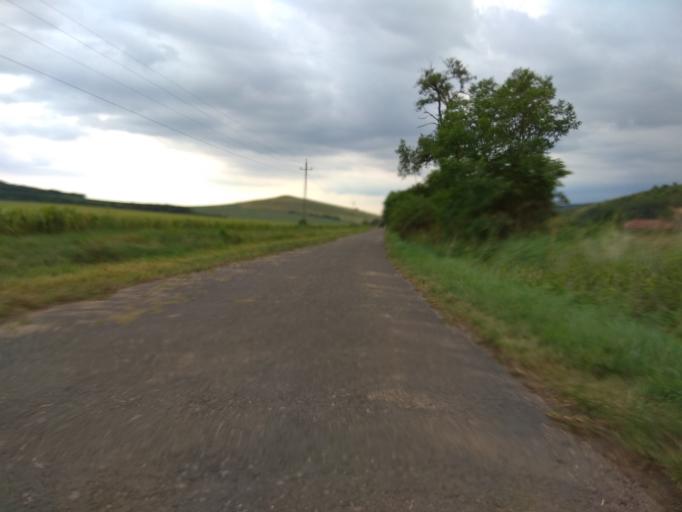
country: HU
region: Borsod-Abauj-Zemplen
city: Monok
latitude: 48.1899
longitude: 21.1256
